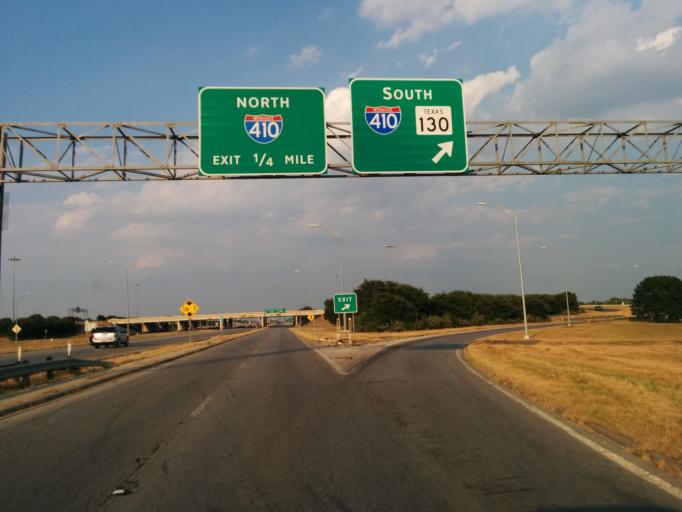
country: US
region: Texas
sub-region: Bexar County
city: Kirby
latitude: 29.4346
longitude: -98.3933
